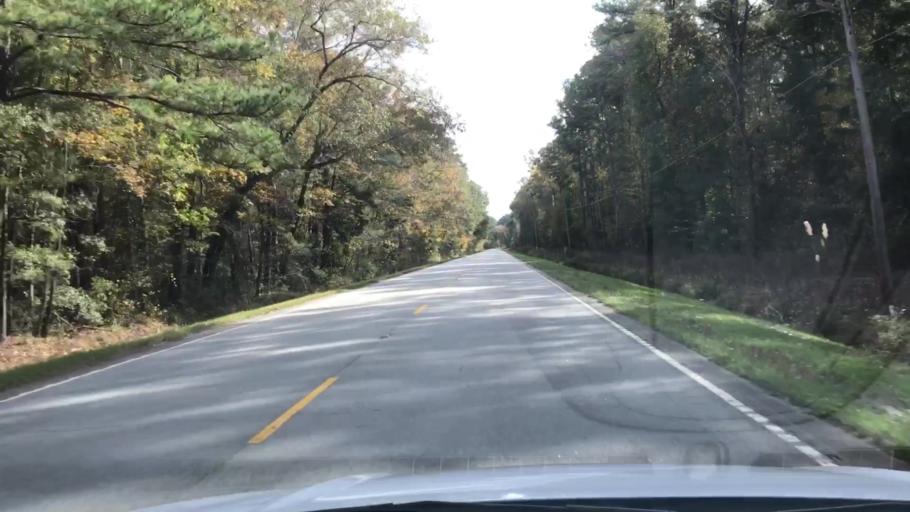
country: US
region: South Carolina
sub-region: Colleton County
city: Walterboro
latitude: 32.7995
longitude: -80.4980
